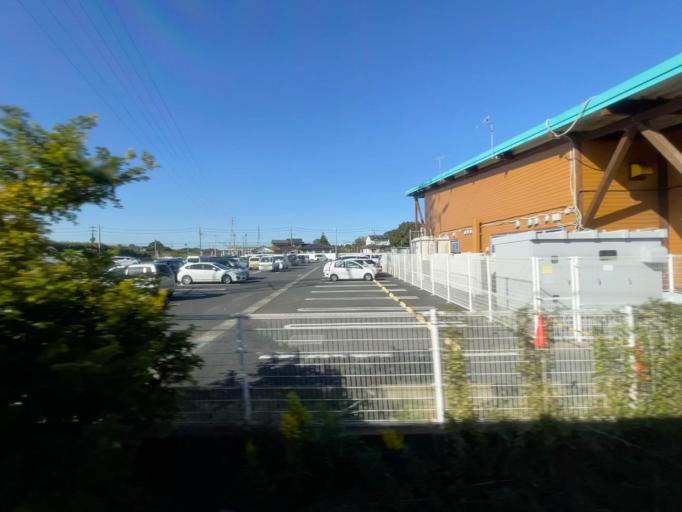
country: JP
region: Chiba
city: Yokaichiba
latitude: 35.7133
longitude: 140.5826
